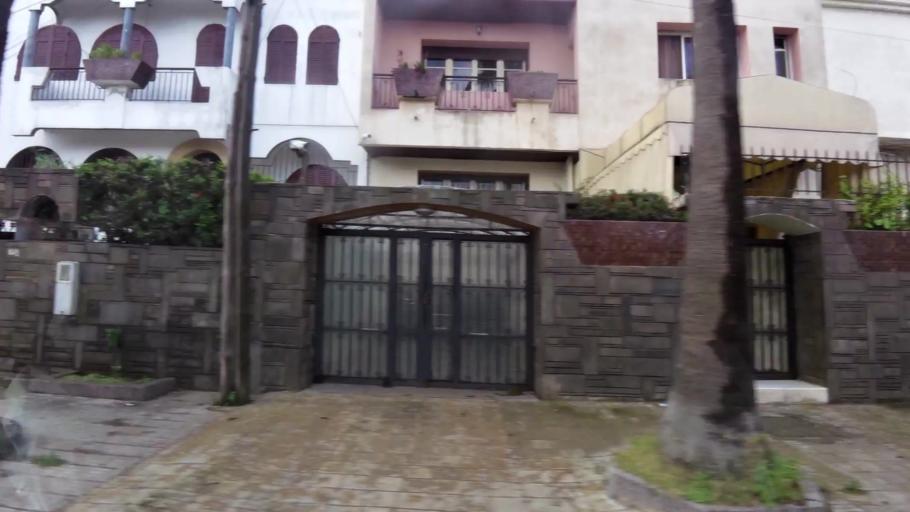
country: MA
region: Grand Casablanca
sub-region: Casablanca
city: Casablanca
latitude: 33.5640
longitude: -7.6798
